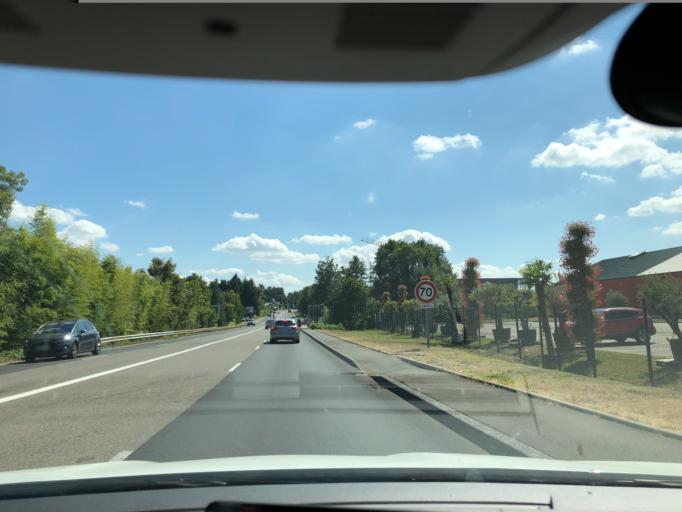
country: FR
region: Rhone-Alpes
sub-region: Departement du Rhone
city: Limonest
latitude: 45.8180
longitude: 4.7716
